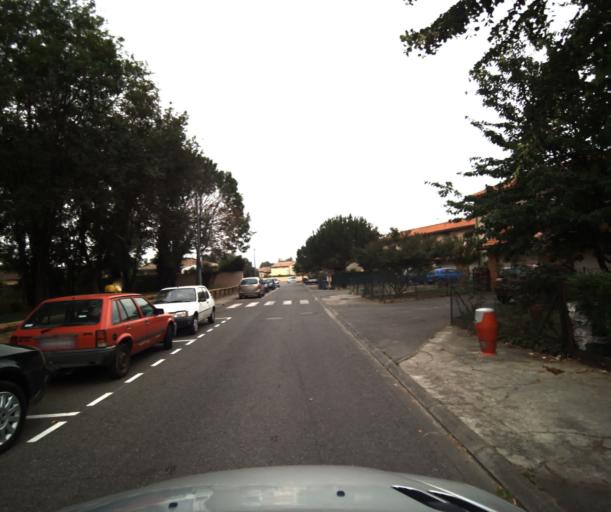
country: FR
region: Midi-Pyrenees
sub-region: Departement de la Haute-Garonne
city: Portet-sur-Garonne
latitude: 43.5320
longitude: 1.4154
